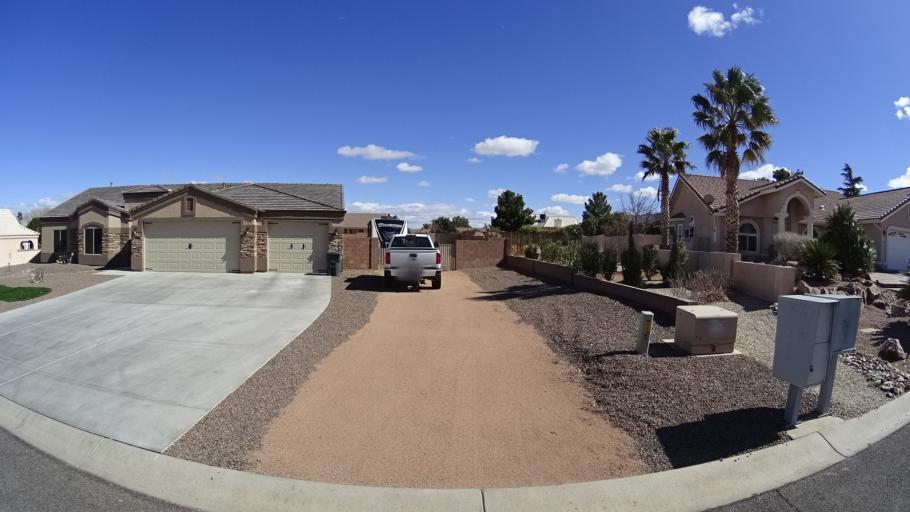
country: US
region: Arizona
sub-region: Mohave County
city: Kingman
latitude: 35.2010
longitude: -113.9730
